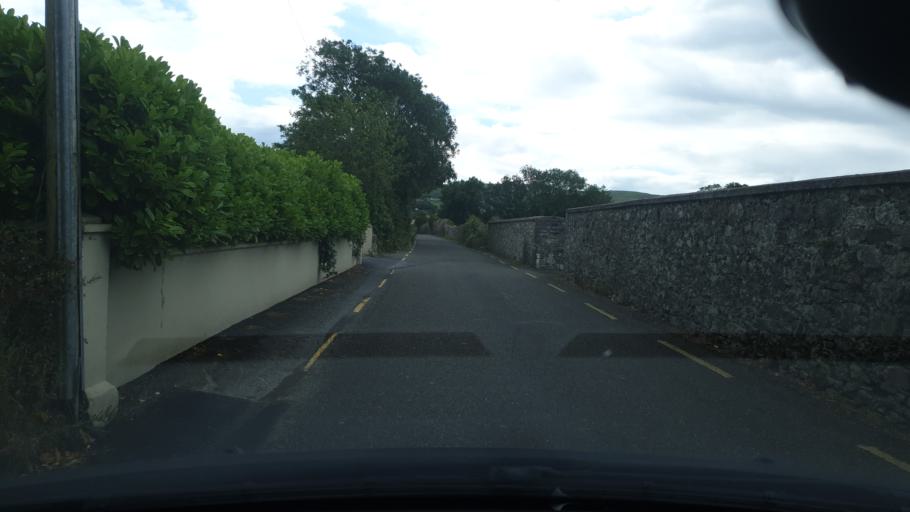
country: IE
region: Munster
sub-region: Ciarrai
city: Tralee
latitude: 52.2520
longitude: -9.6450
